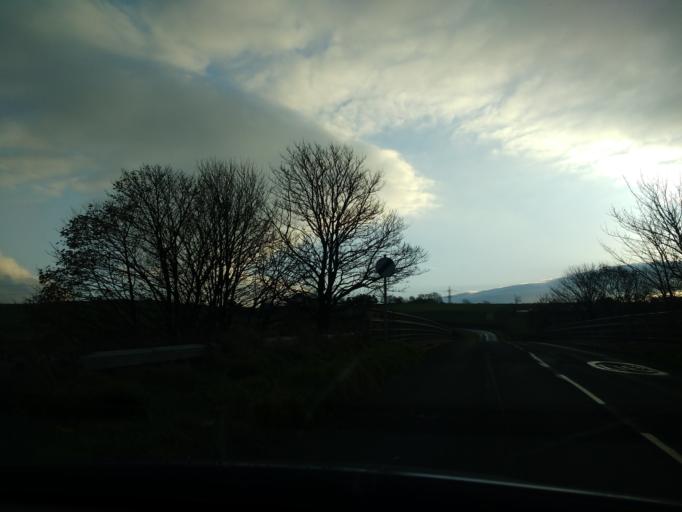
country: GB
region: England
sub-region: Lancashire
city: Lancaster
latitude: 54.0459
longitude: -2.7672
